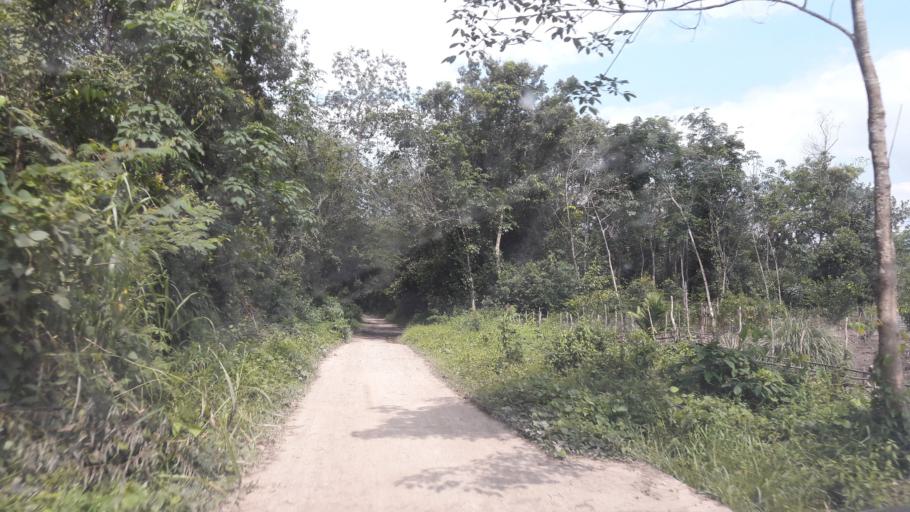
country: ID
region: South Sumatra
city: Gunungmenang
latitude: -3.3447
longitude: 104.0808
